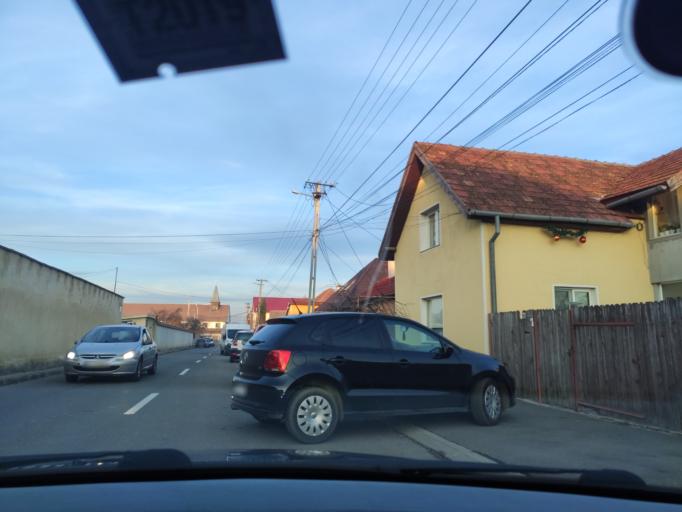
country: RO
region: Brasov
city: Codlea
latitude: 45.6926
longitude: 25.4511
